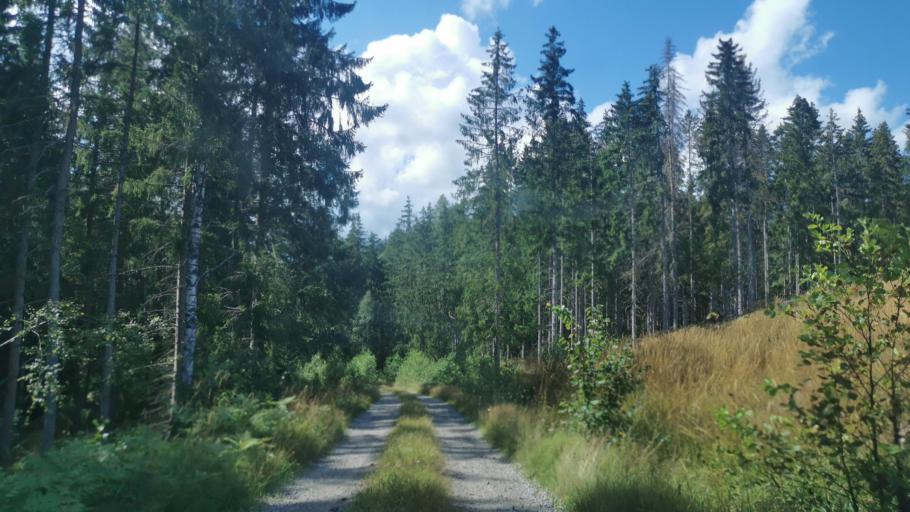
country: SE
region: OEstergoetland
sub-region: Finspangs Kommun
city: Finspang
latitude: 58.8013
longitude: 15.8061
